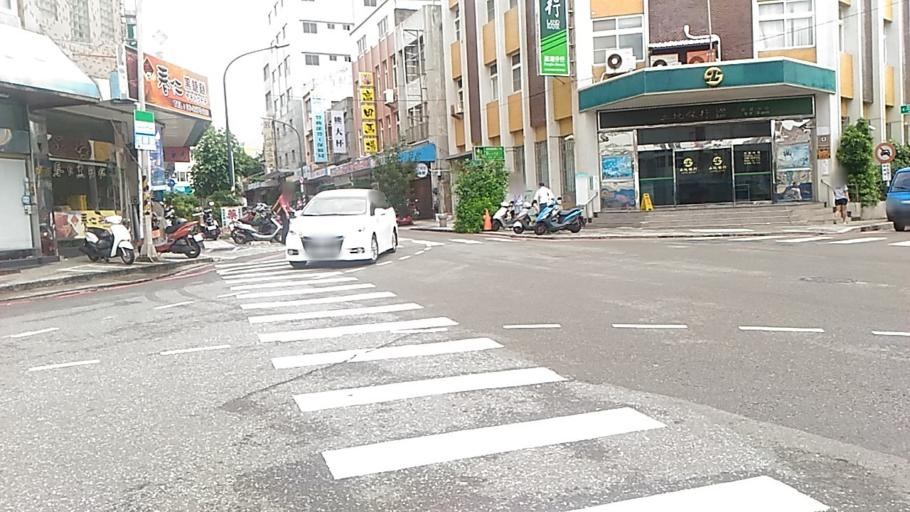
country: TW
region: Taiwan
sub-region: Penghu
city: Ma-kung
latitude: 23.5666
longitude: 119.5686
